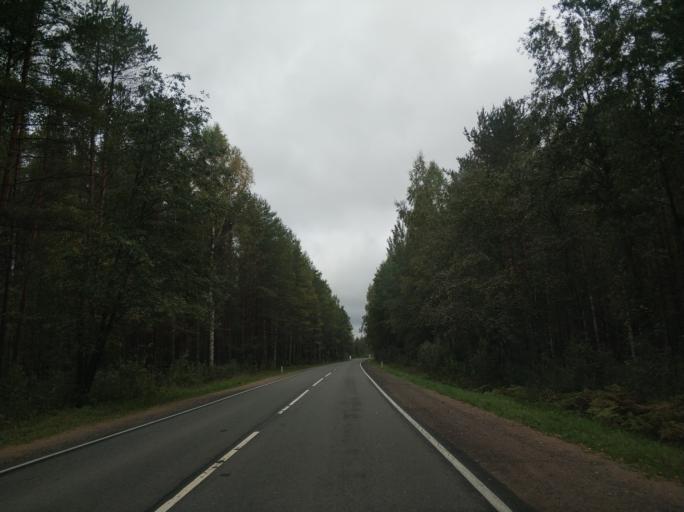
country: RU
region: Leningrad
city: Borisova Griva
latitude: 60.0905
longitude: 30.8598
